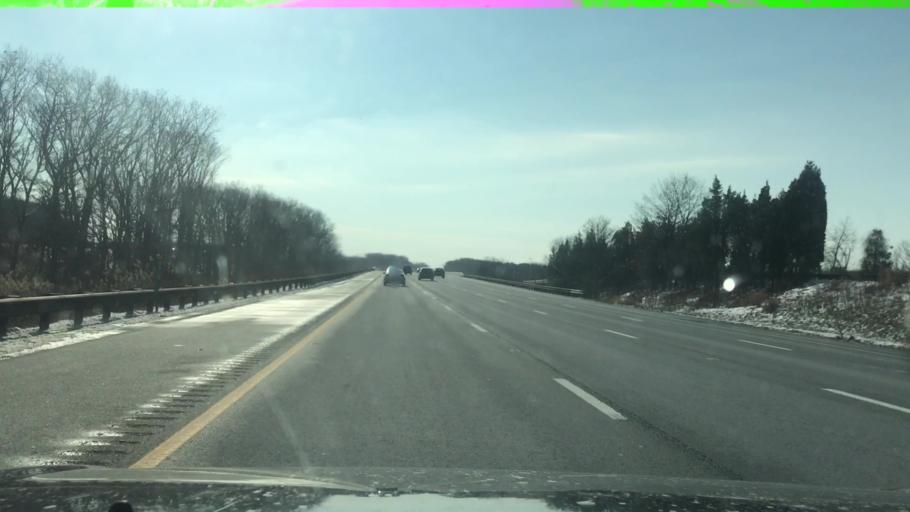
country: US
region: New Jersey
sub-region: Monmouth County
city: Shark River Hills
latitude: 40.1656
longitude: -74.1020
